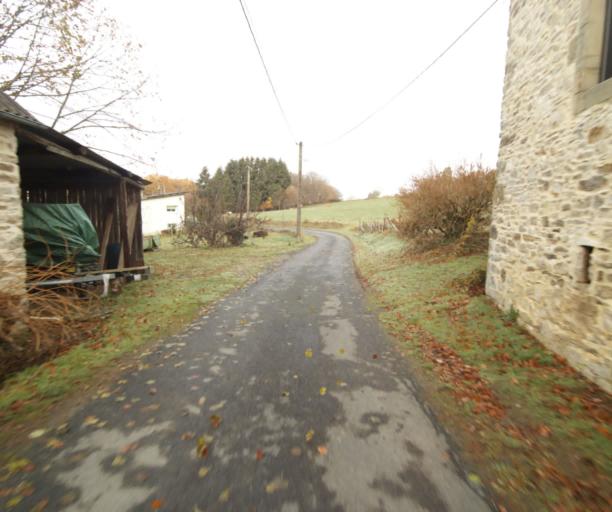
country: FR
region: Limousin
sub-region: Departement de la Correze
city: Cornil
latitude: 45.1990
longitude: 1.7130
